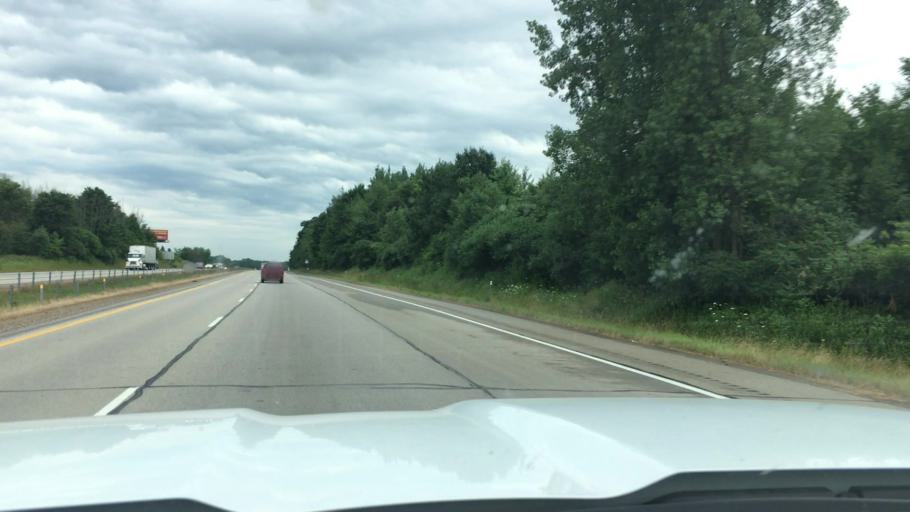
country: US
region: Michigan
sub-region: Allegan County
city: Wayland
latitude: 42.7215
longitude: -85.6706
